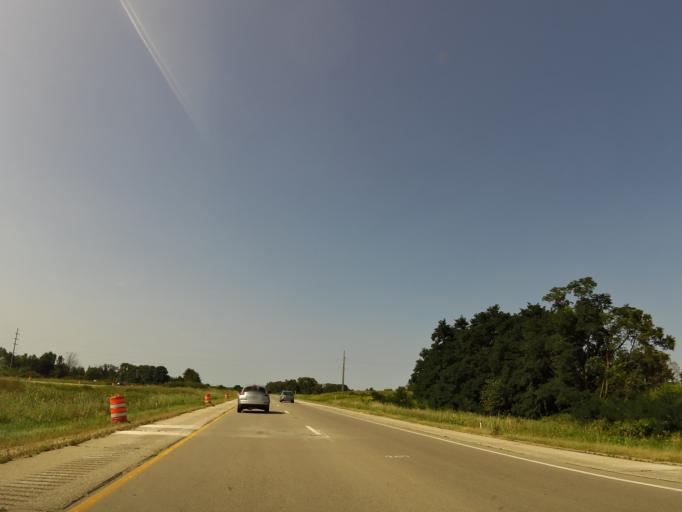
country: US
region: Wisconsin
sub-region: Juneau County
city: Mauston
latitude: 43.8364
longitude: -90.0921
